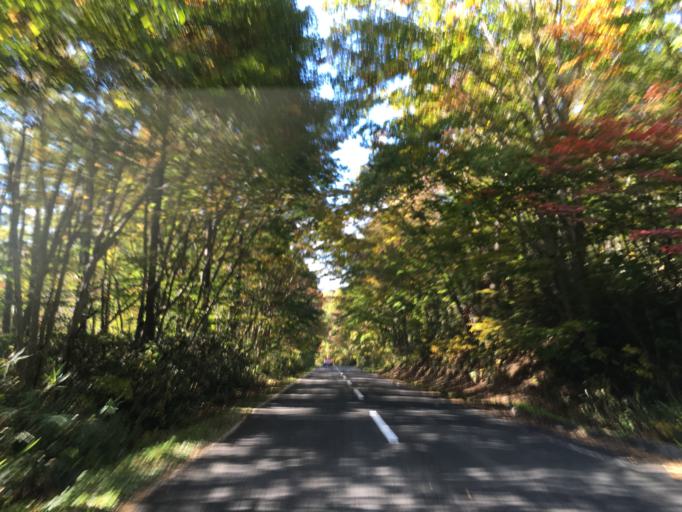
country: JP
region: Fukushima
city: Inawashiro
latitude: 37.6476
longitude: 140.2119
